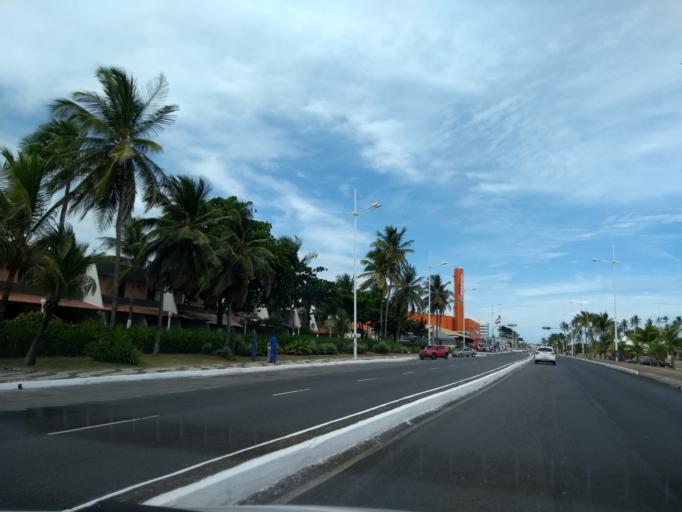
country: BR
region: Bahia
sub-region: Lauro De Freitas
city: Lauro de Freitas
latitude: -12.9538
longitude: -38.3810
